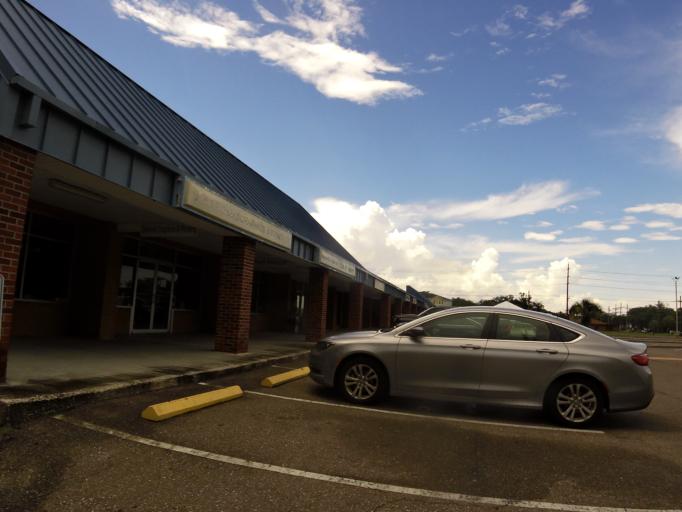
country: US
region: Florida
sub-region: Duval County
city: Jacksonville
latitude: 30.3712
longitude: -81.6577
